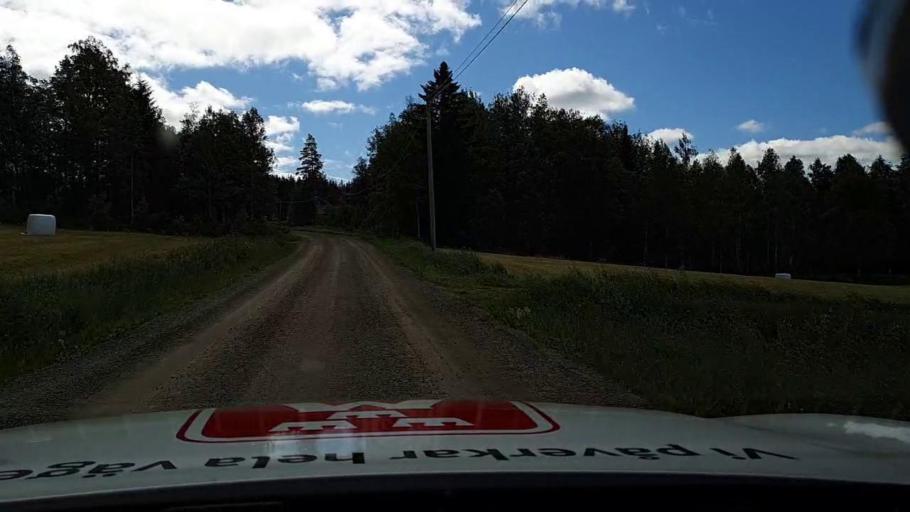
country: SE
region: Jaemtland
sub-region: Braecke Kommun
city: Braecke
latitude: 62.7750
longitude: 15.4794
